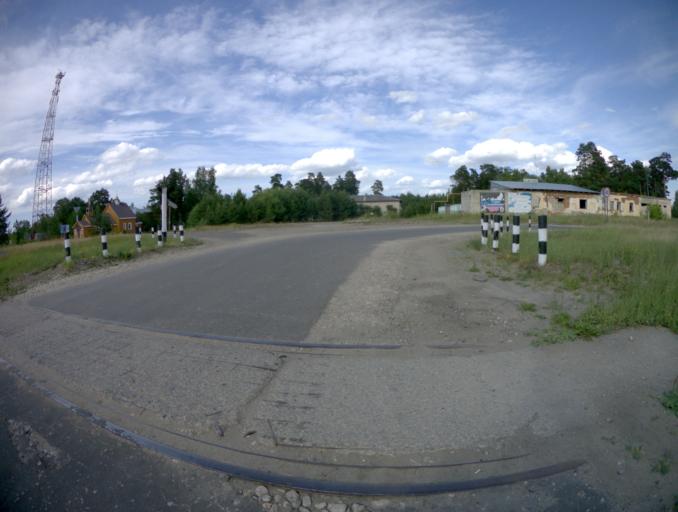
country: RU
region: Vladimir
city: Gorokhovets
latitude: 56.2939
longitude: 42.7858
